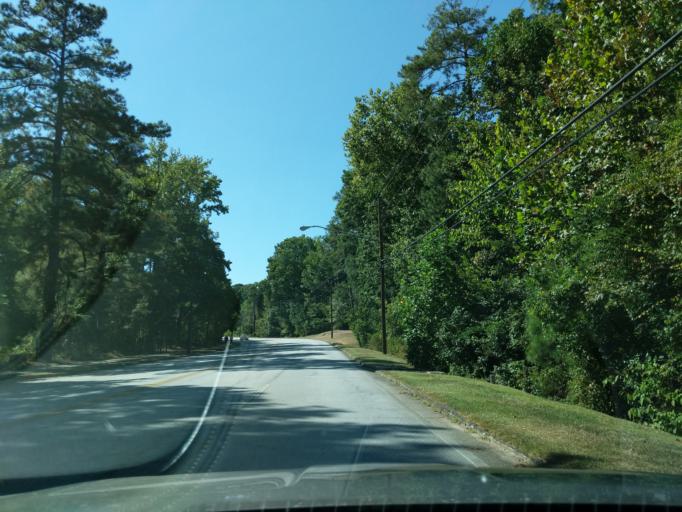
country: US
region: Georgia
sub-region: DeKalb County
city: Stone Mountain
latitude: 33.8128
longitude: -84.1552
